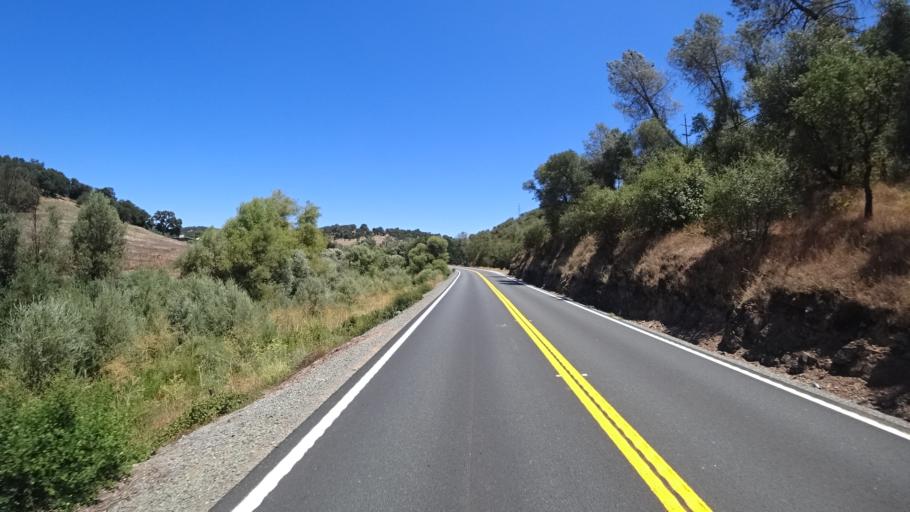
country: US
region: California
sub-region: Calaveras County
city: San Andreas
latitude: 38.2077
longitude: -120.7019
